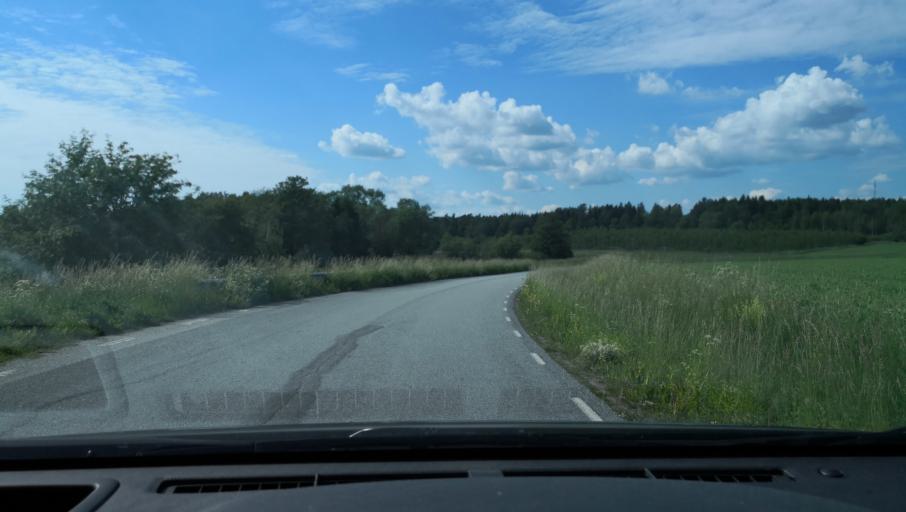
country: SE
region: Uppsala
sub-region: Enkopings Kommun
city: Orsundsbro
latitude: 59.8147
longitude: 17.3702
